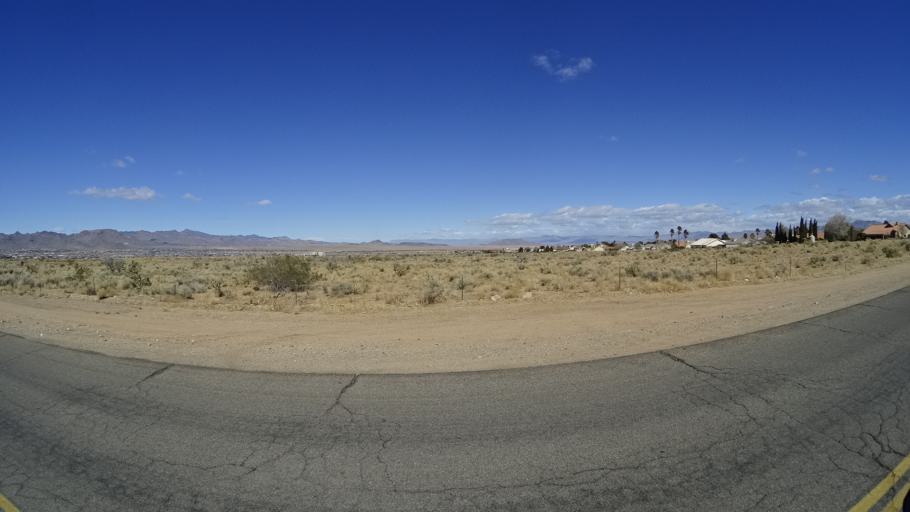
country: US
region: Arizona
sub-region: Mohave County
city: Kingman
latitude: 35.1958
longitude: -113.9775
